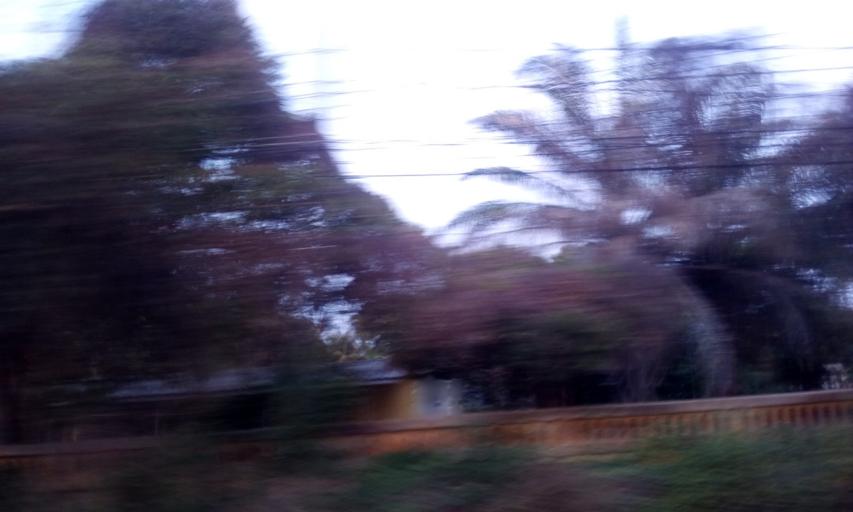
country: TH
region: Trat
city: Laem Ngop
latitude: 12.2472
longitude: 102.2936
